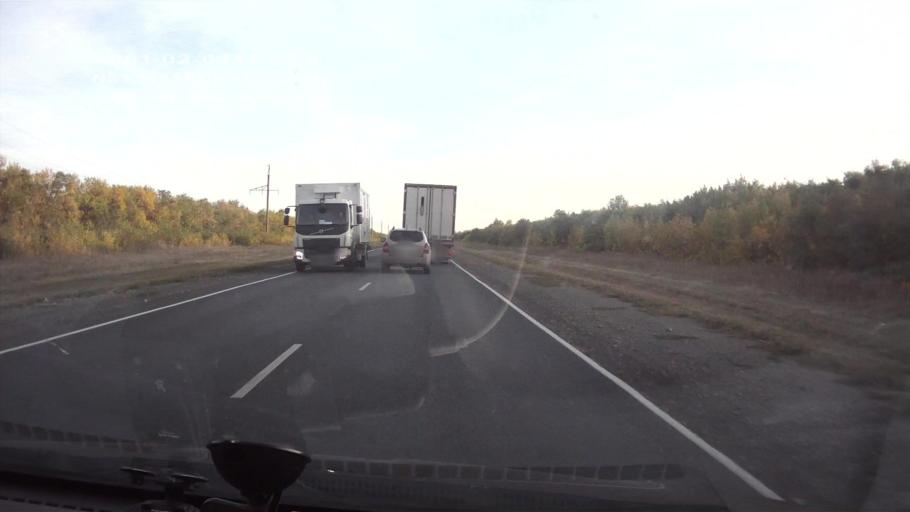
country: RU
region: Saratov
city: Krasnoarmeysk
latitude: 51.1356
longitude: 45.6502
